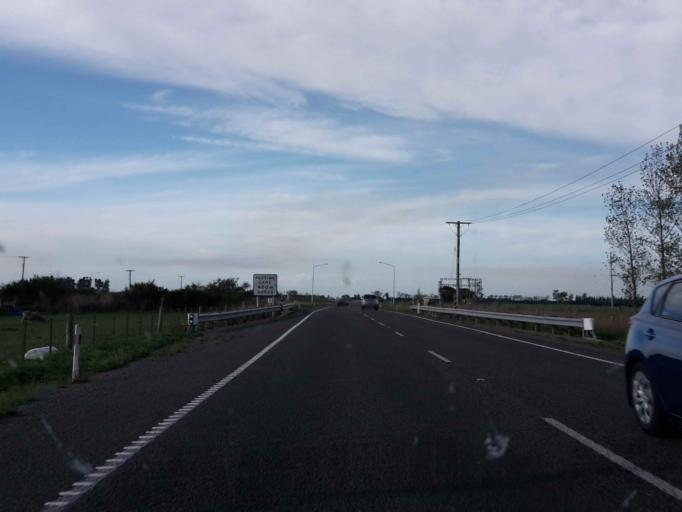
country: NZ
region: Canterbury
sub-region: Ashburton District
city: Tinwald
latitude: -43.9912
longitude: 171.5890
